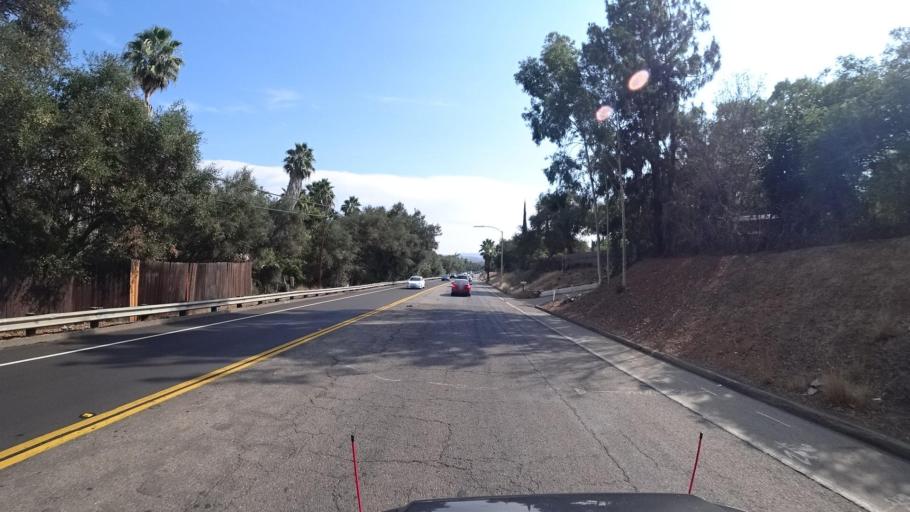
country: US
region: California
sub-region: San Diego County
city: Escondido
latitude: 33.0921
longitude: -117.0587
